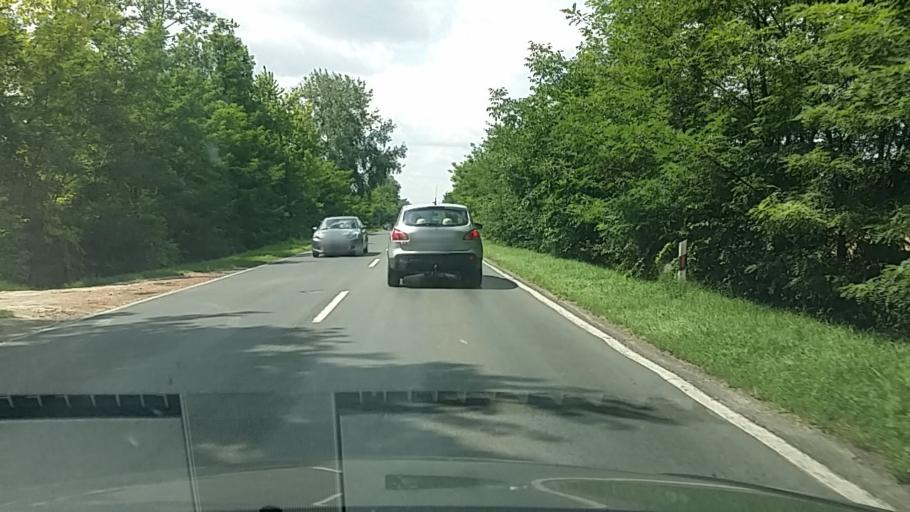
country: HU
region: Bacs-Kiskun
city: Lajosmizse
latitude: 46.9985
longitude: 19.5981
